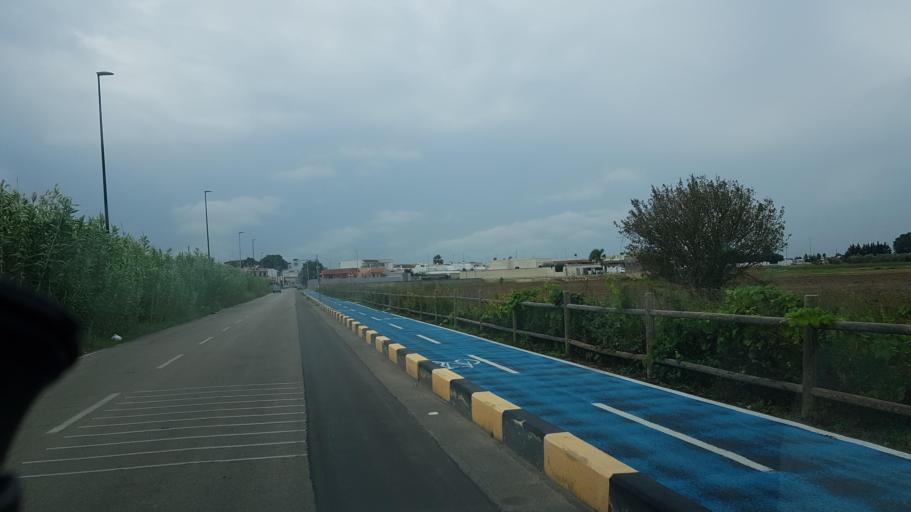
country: IT
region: Apulia
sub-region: Provincia di Lecce
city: Guagnano
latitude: 40.4072
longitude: 17.9542
